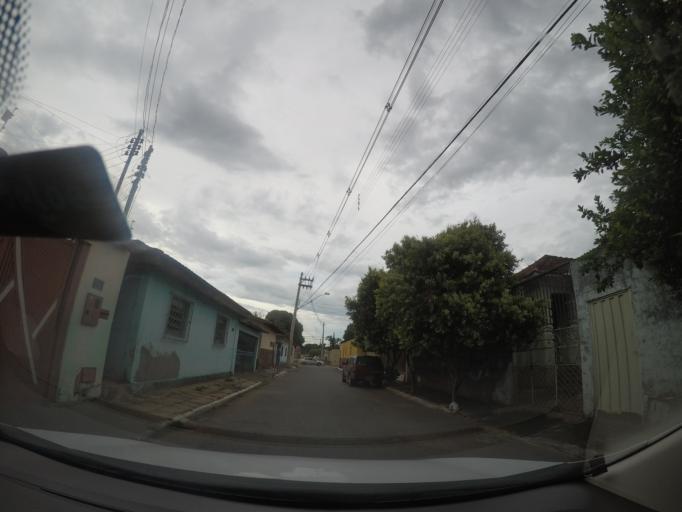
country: BR
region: Goias
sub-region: Goiania
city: Goiania
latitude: -16.6648
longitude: -49.2953
